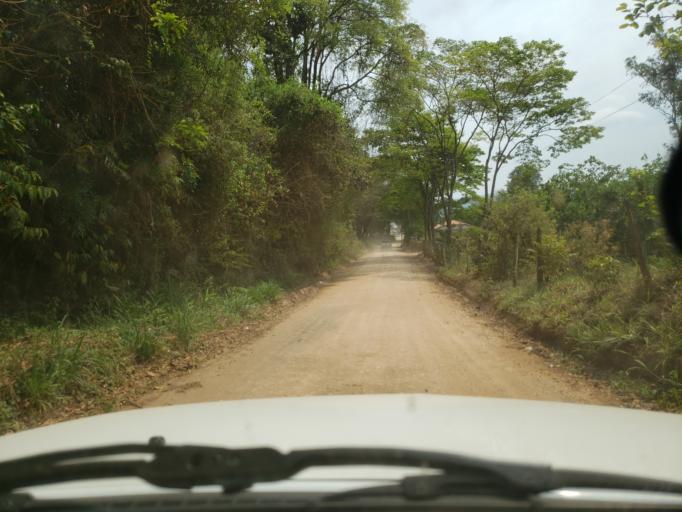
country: BR
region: Minas Gerais
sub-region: Jacutinga
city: Jacutinga
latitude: -22.3055
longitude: -46.6083
